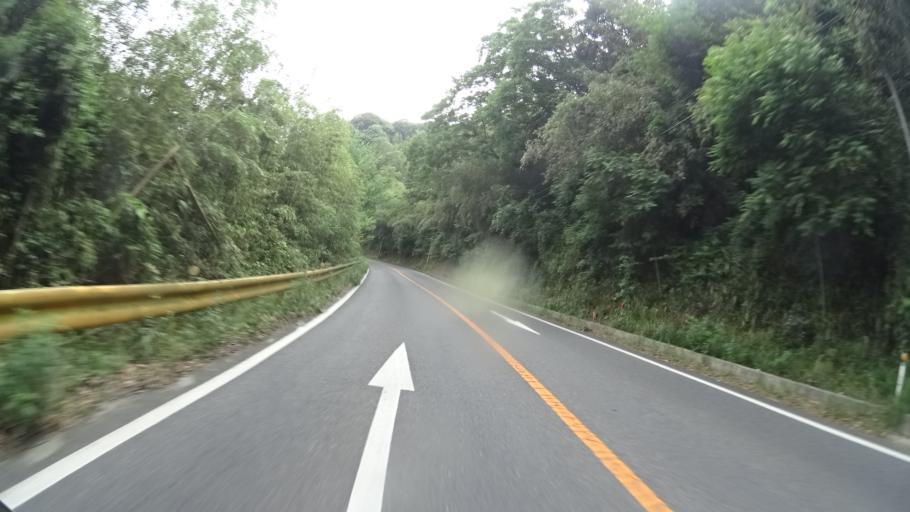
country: JP
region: Yamaguchi
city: Nagato
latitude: 34.2105
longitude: 131.0700
